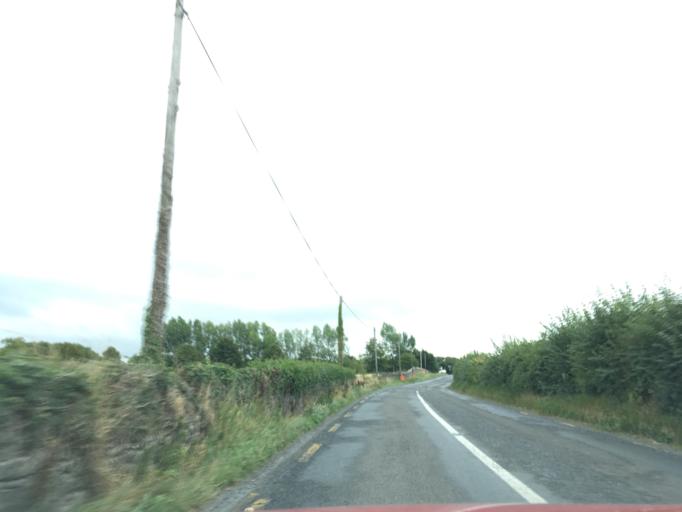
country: IE
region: Munster
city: Cashel
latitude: 52.4462
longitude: -7.8057
